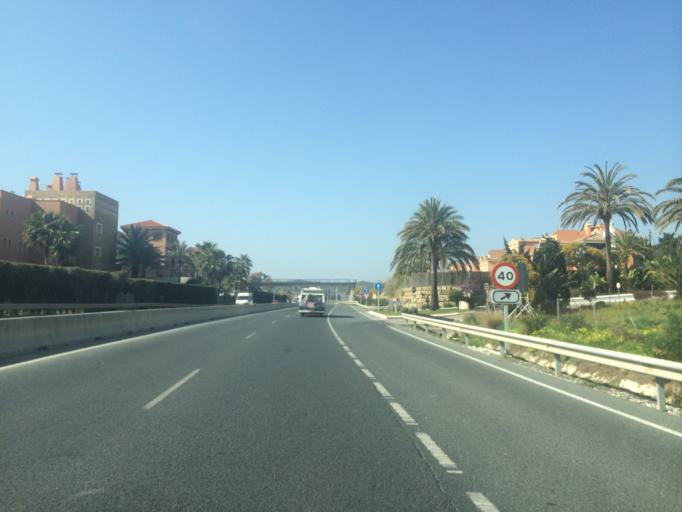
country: ES
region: Andalusia
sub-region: Provincia de Malaga
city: Estepona
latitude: 36.4096
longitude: -5.1854
